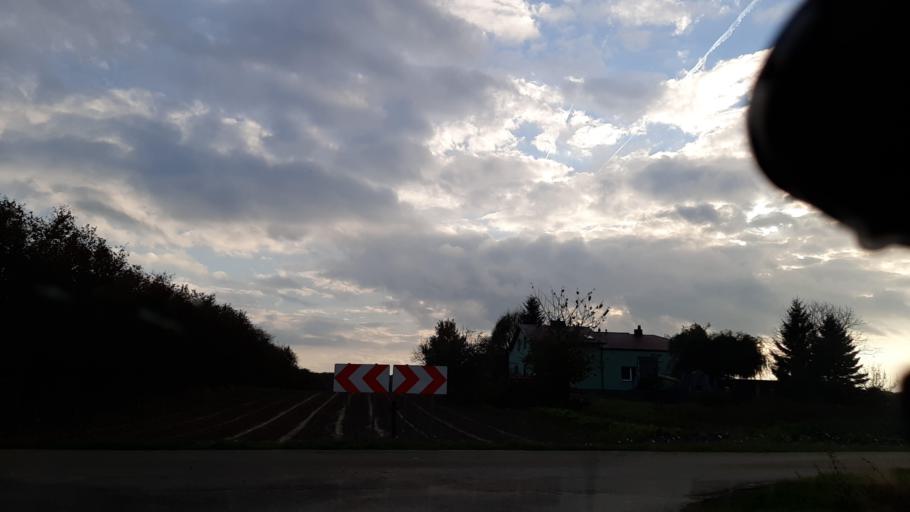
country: PL
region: Lublin Voivodeship
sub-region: Powiat lubelski
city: Garbow
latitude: 51.3388
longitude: 22.3195
